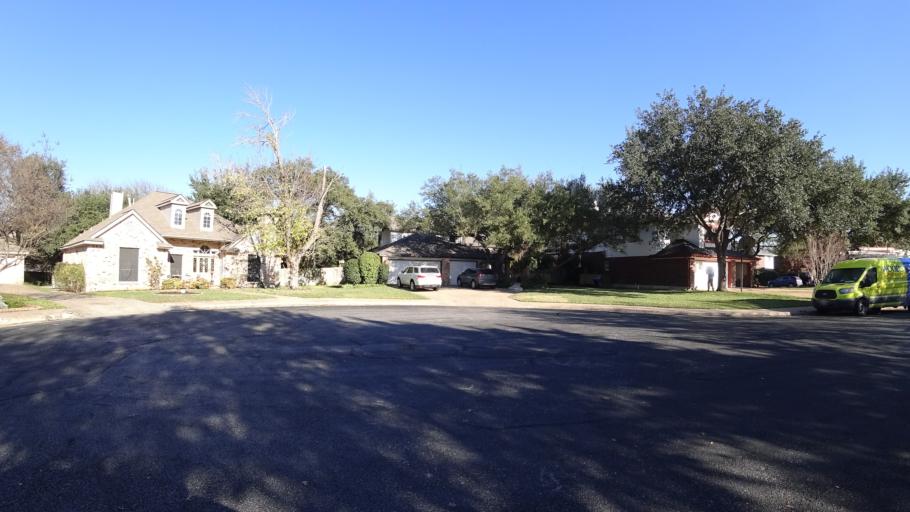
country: US
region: Texas
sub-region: Williamson County
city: Brushy Creek
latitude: 30.4899
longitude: -97.7437
